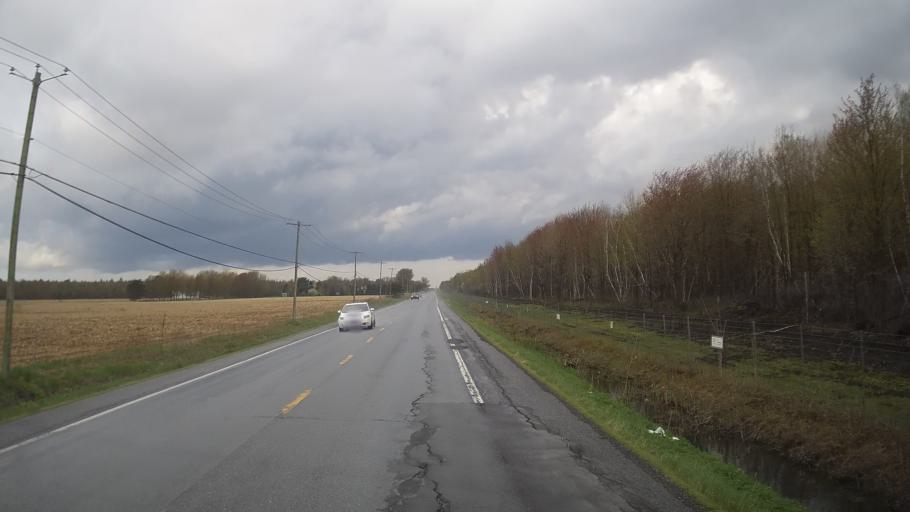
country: CA
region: Quebec
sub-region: Monteregie
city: Farnham
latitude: 45.2958
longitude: -73.0255
